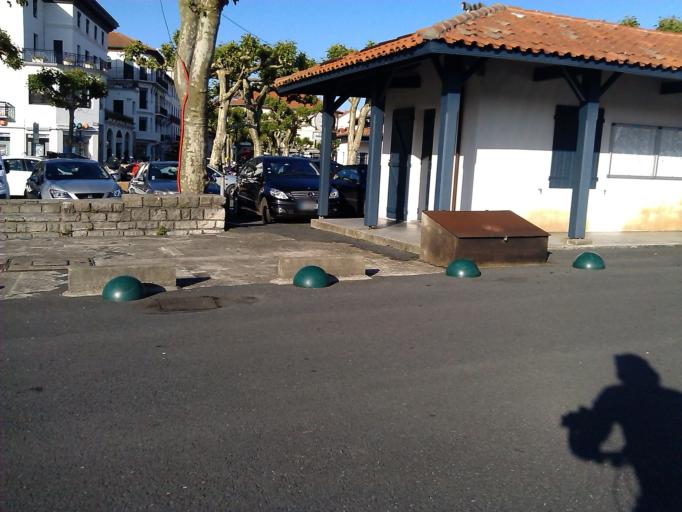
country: FR
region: Aquitaine
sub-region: Departement des Pyrenees-Atlantiques
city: Saint-Jean-de-Luz
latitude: 43.3871
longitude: -1.6640
